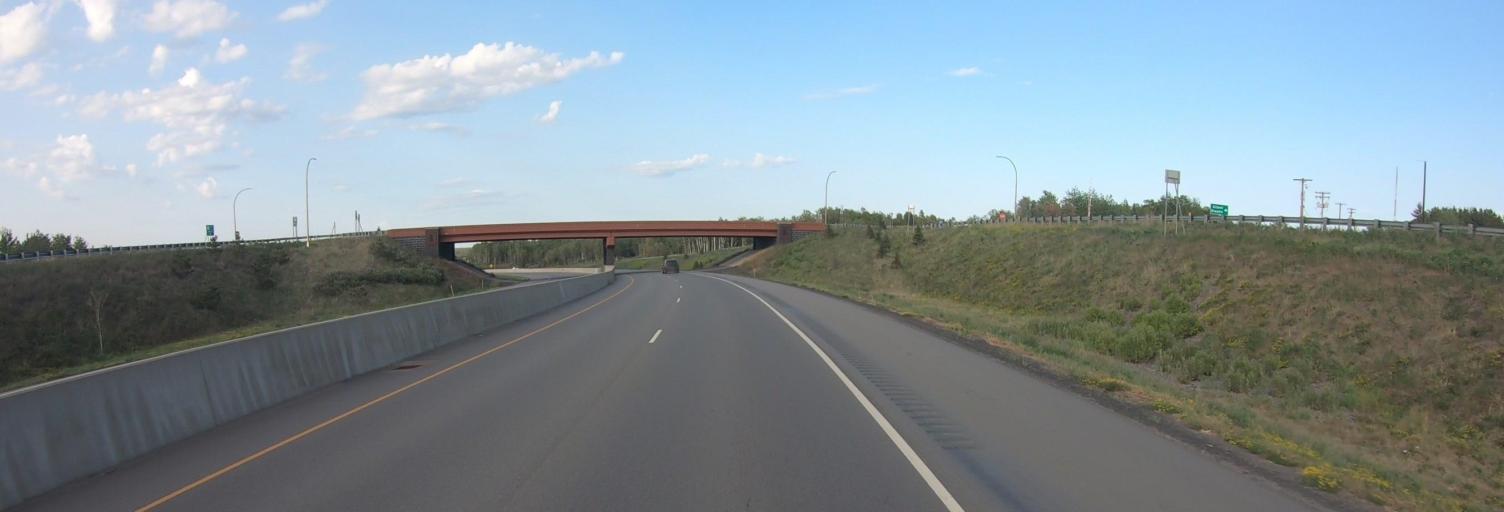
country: US
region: Minnesota
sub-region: Saint Louis County
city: Virginia
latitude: 47.5012
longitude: -92.5193
